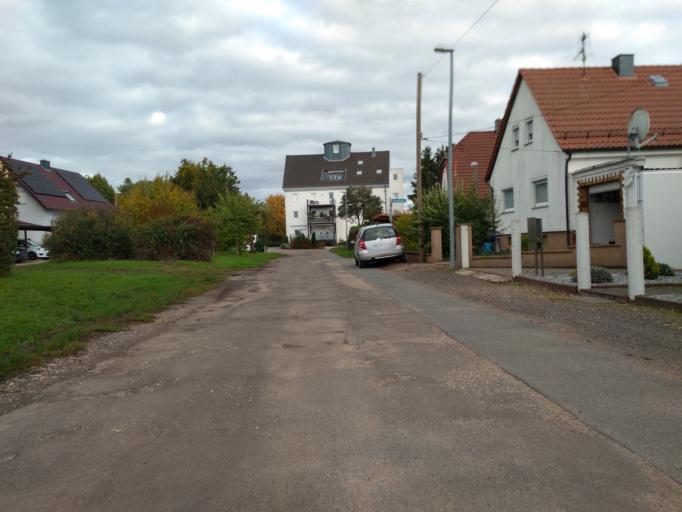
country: DE
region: Rheinland-Pfalz
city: Offstein
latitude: 49.6068
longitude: 8.2615
